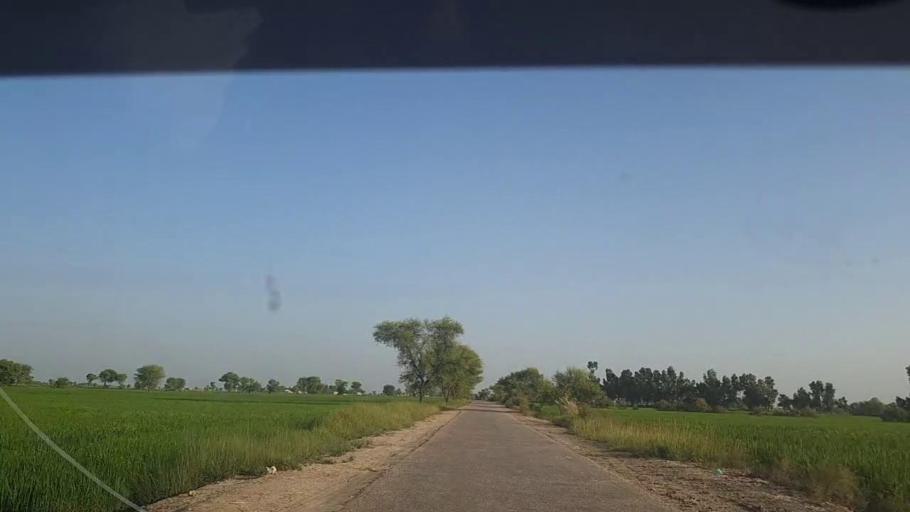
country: PK
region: Sindh
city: Thul
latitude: 28.2068
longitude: 68.8715
